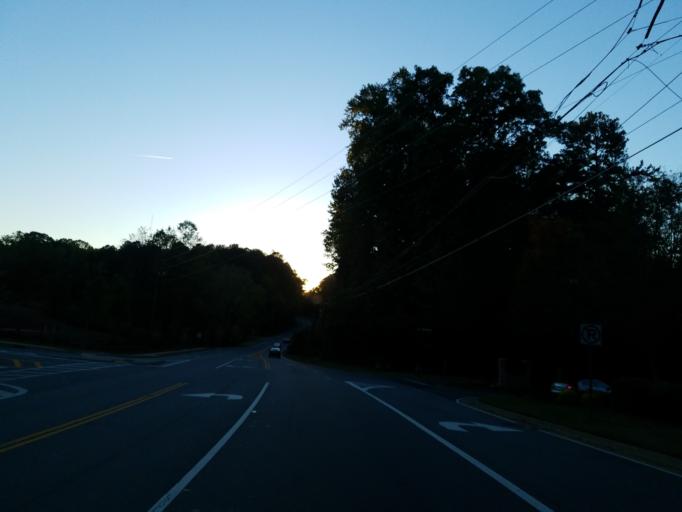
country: US
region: Georgia
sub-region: Forsyth County
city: Cumming
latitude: 34.1801
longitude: -84.1523
